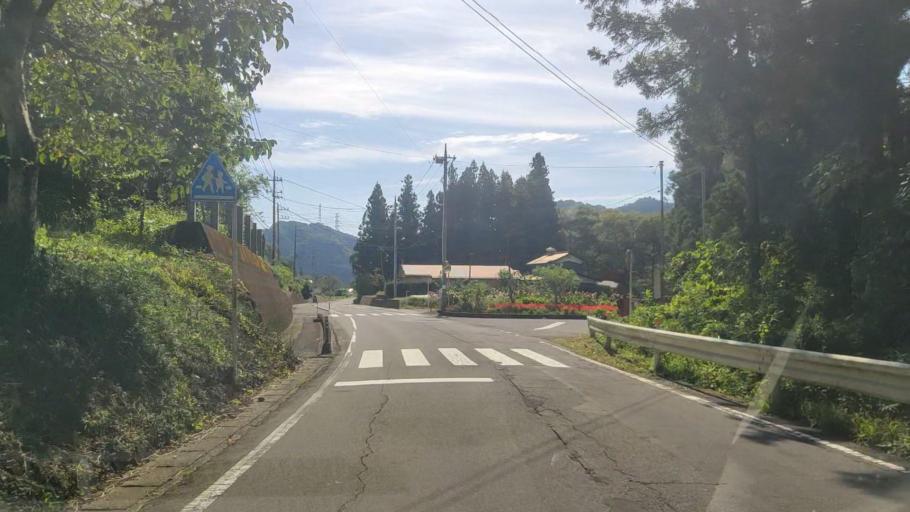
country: JP
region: Gunma
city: Nakanojomachi
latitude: 36.6137
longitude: 138.7820
